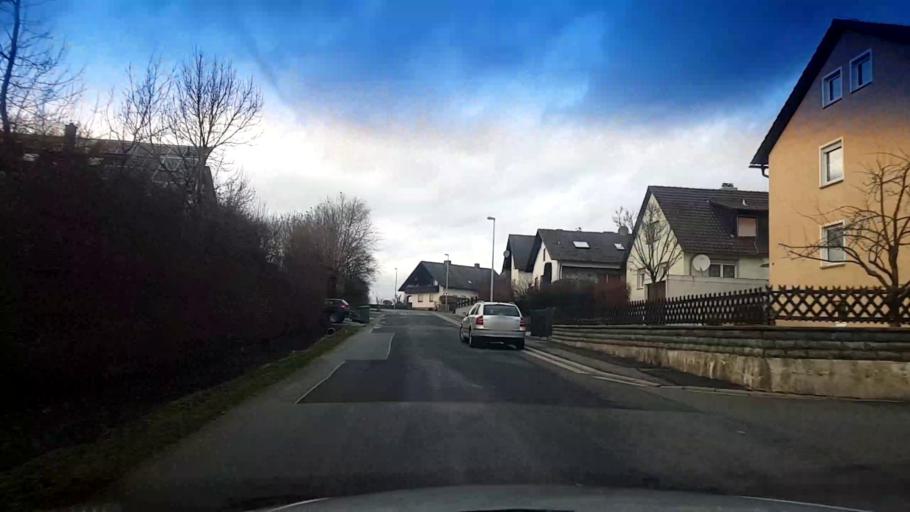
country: DE
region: Bavaria
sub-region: Upper Franconia
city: Strullendorf
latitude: 49.8606
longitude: 11.0074
